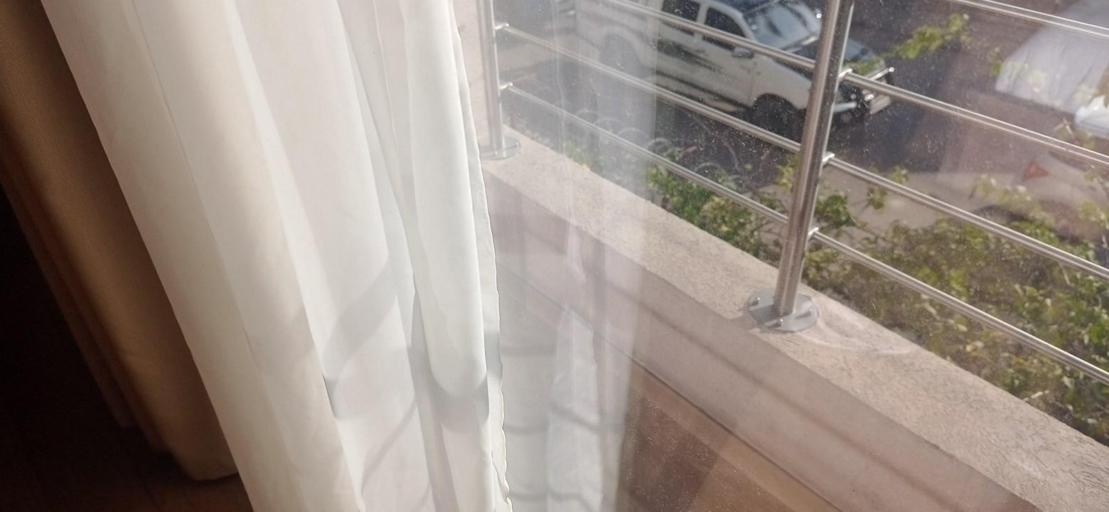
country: CD
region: Kinshasa
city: Kinshasa
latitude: -4.3043
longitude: 15.3032
